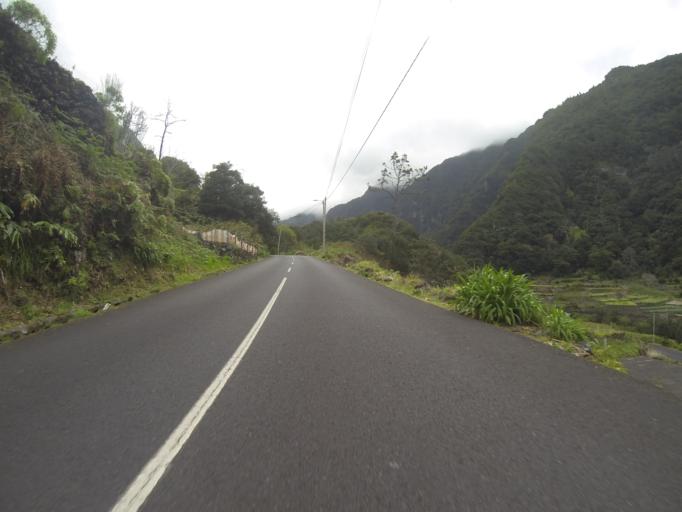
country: PT
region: Madeira
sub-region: Porto Moniz
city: Porto Moniz
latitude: 32.8124
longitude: -17.1110
